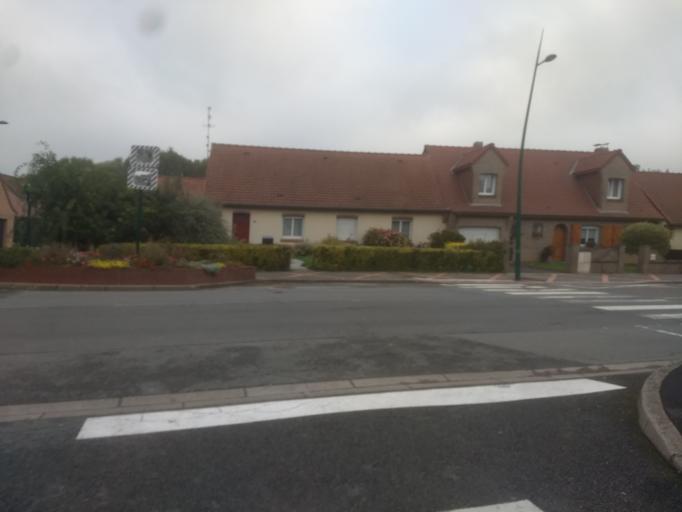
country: FR
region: Nord-Pas-de-Calais
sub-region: Departement du Pas-de-Calais
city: Saint-Laurent-Blangy
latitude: 50.2966
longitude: 2.7980
